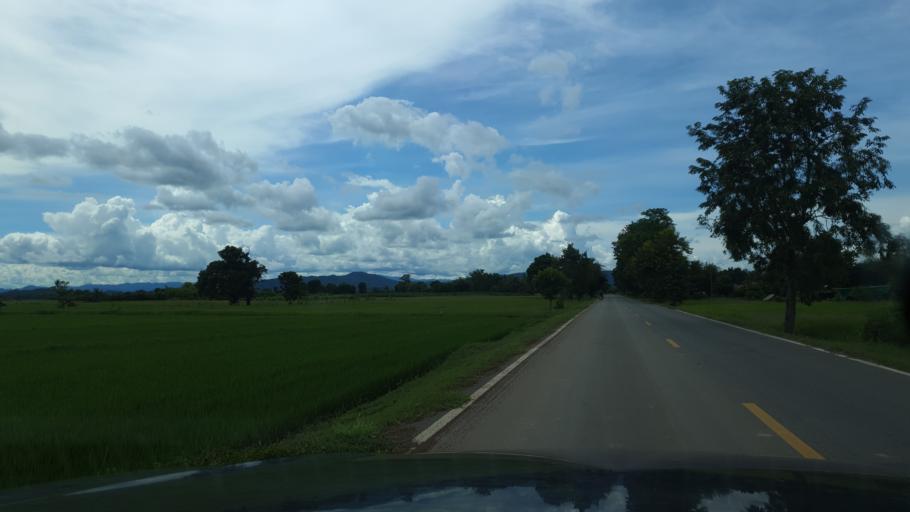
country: TH
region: Sukhothai
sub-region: Amphoe Si Satchanalai
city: Si Satchanalai
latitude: 17.4627
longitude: 99.7612
